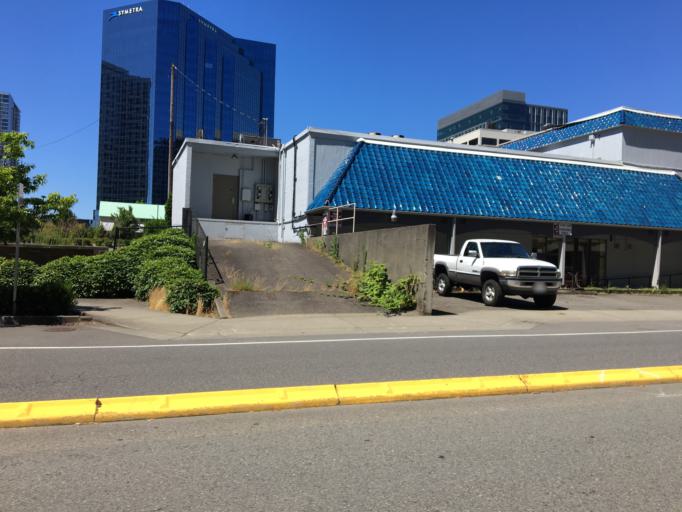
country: US
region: Washington
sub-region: King County
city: Bellevue
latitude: 47.6165
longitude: -122.1935
